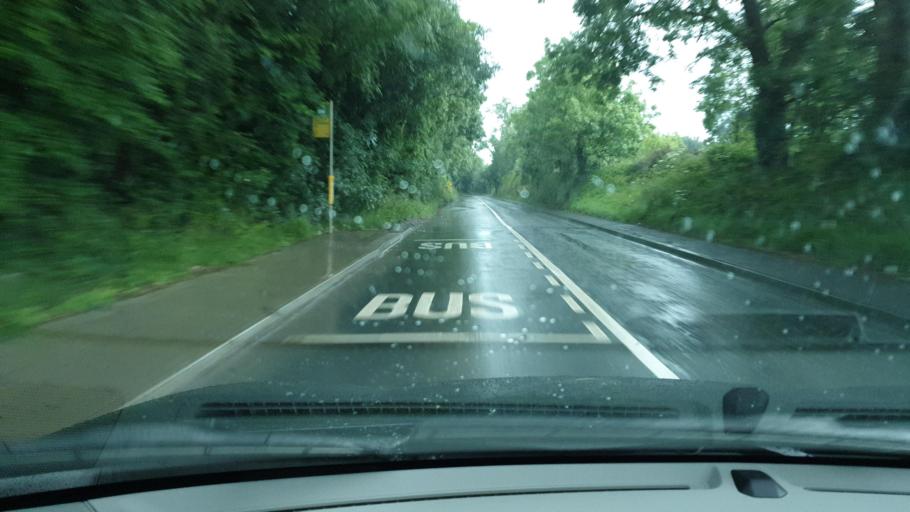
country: IE
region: Leinster
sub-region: An Mhi
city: Navan
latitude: 53.6360
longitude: -6.6881
